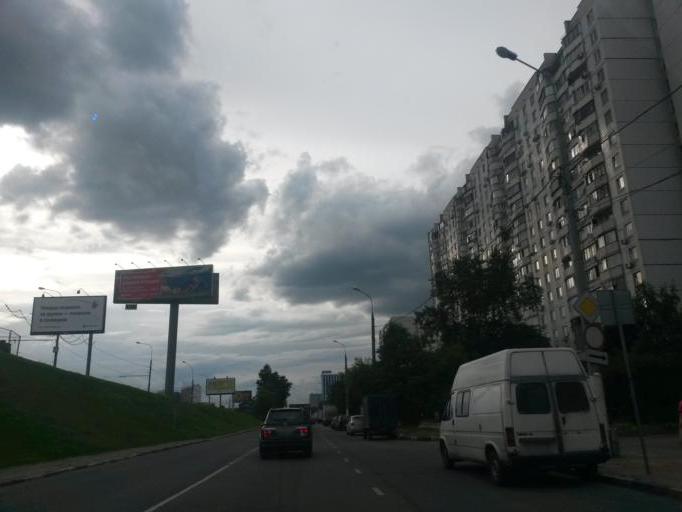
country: RU
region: Moskovskaya
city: Kur'yanovo
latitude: 55.6371
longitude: 37.6949
